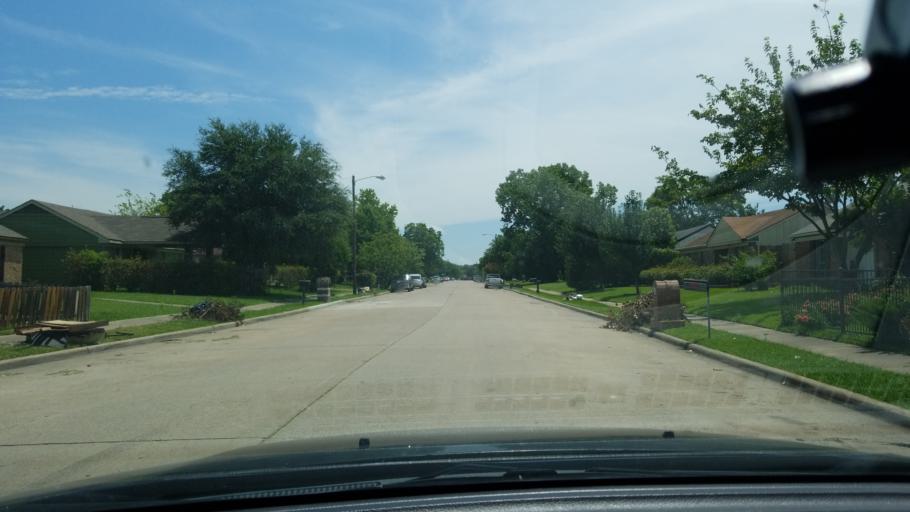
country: US
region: Texas
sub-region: Dallas County
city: Balch Springs
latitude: 32.7426
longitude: -96.6464
